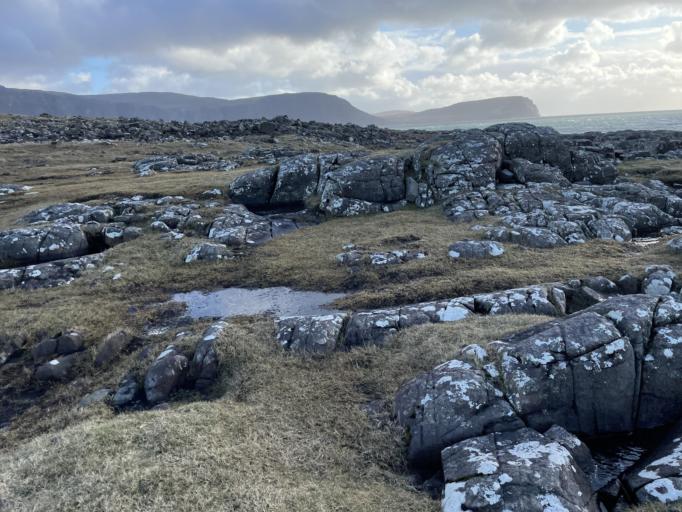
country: GB
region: Scotland
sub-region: Eilean Siar
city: Harris
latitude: 57.4216
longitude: -6.7883
